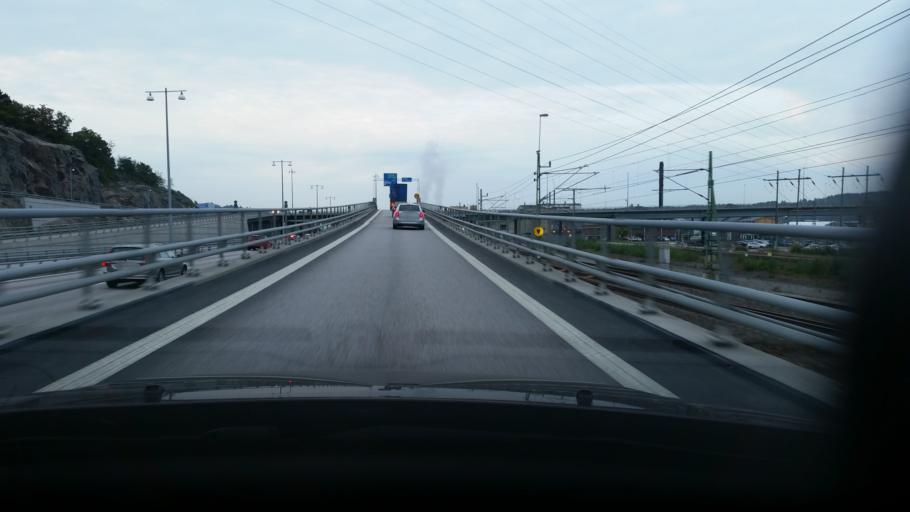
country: SE
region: Vaestra Goetaland
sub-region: Ale Kommun
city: Surte
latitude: 57.8566
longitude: 12.0156
